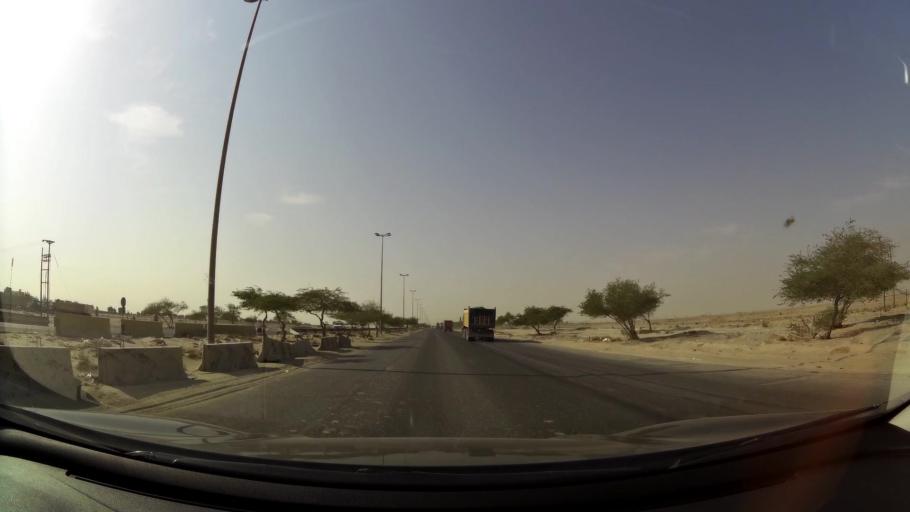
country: KW
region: Al Ahmadi
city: Al Ahmadi
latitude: 28.9441
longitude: 48.1141
